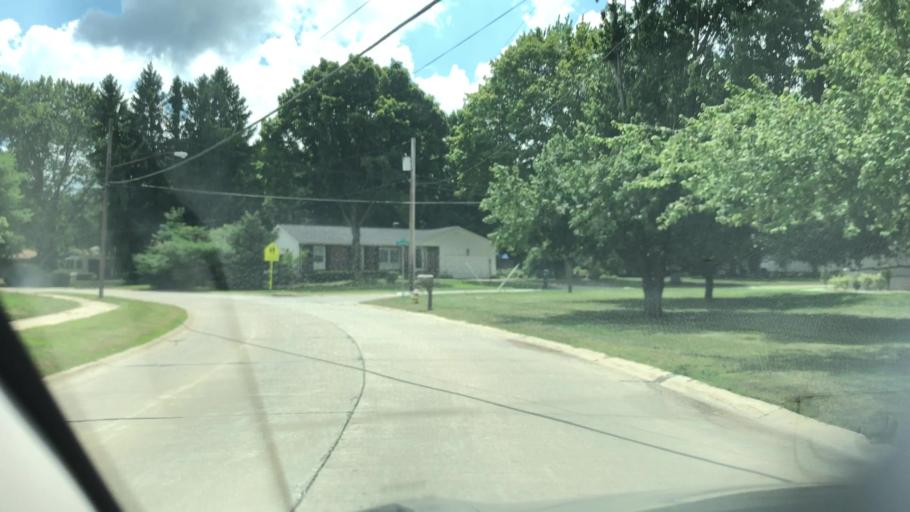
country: US
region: Ohio
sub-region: Summit County
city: Fairlawn
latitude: 41.1241
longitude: -81.6233
